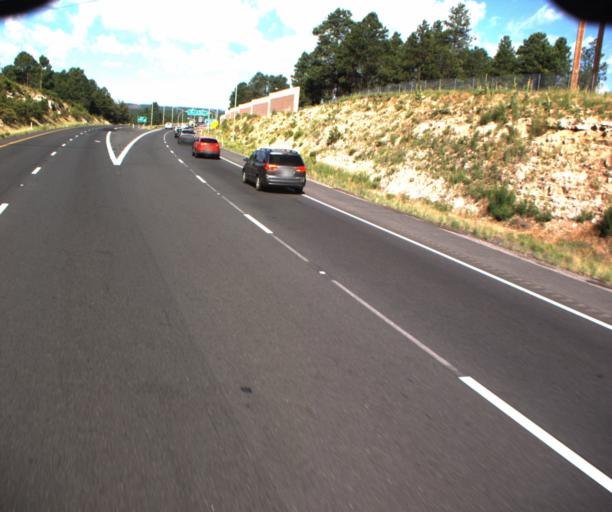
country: US
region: Arizona
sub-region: Coconino County
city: Flagstaff
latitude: 35.1720
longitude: -111.6527
